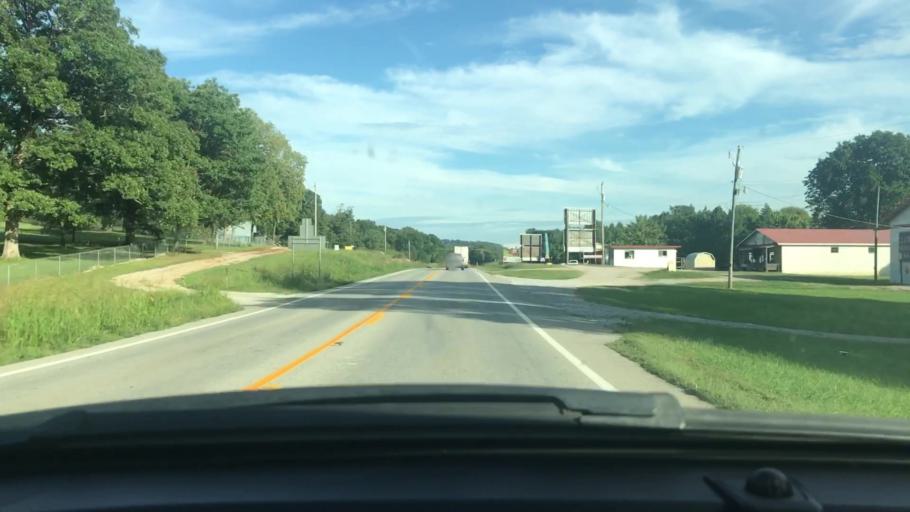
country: US
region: Arkansas
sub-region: Sharp County
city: Cherokee Village
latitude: 36.3014
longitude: -91.4434
